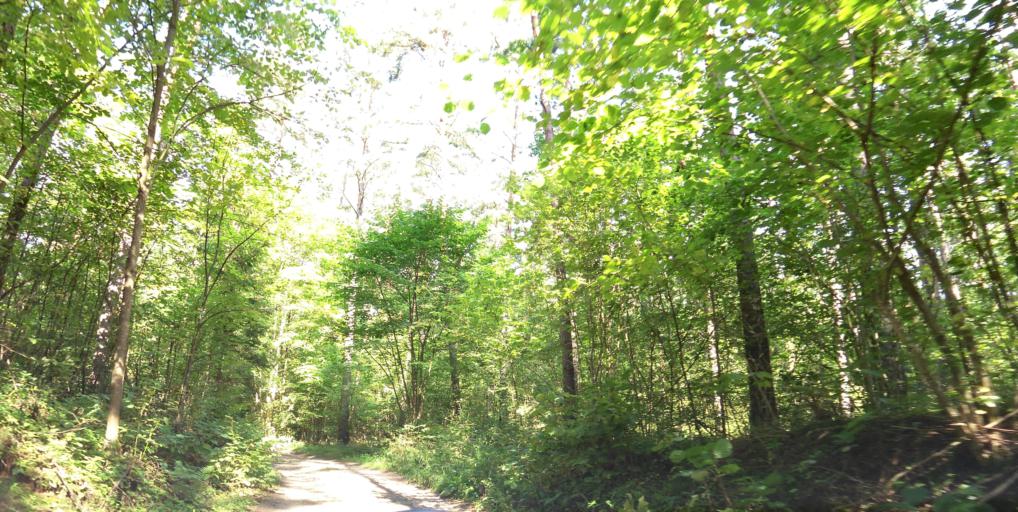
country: LT
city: Grigiskes
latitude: 54.7400
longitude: 25.0328
